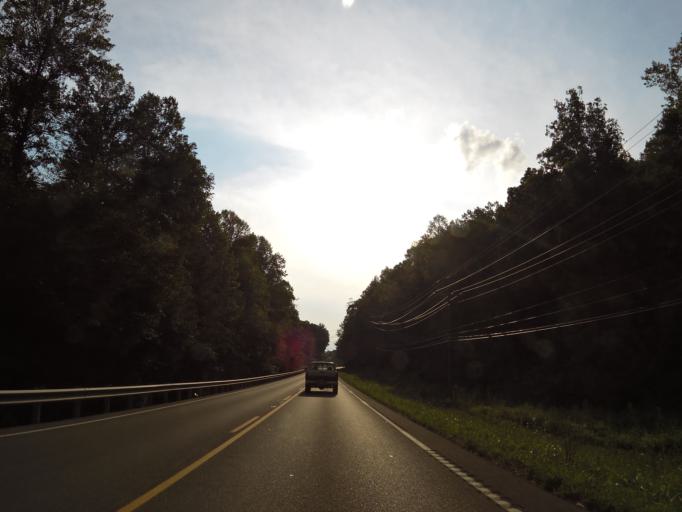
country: US
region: Tennessee
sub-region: Morgan County
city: Coalfield
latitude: 36.0391
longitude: -84.3891
